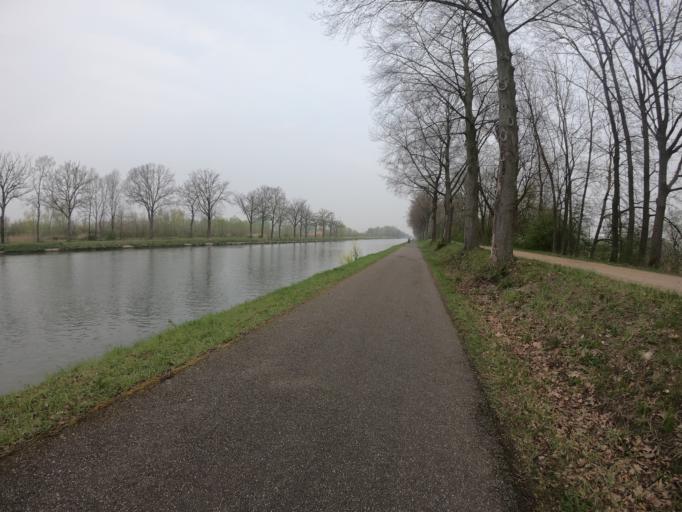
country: BE
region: Flanders
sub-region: Provincie Limburg
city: Maasmechelen
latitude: 50.9295
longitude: 5.7129
